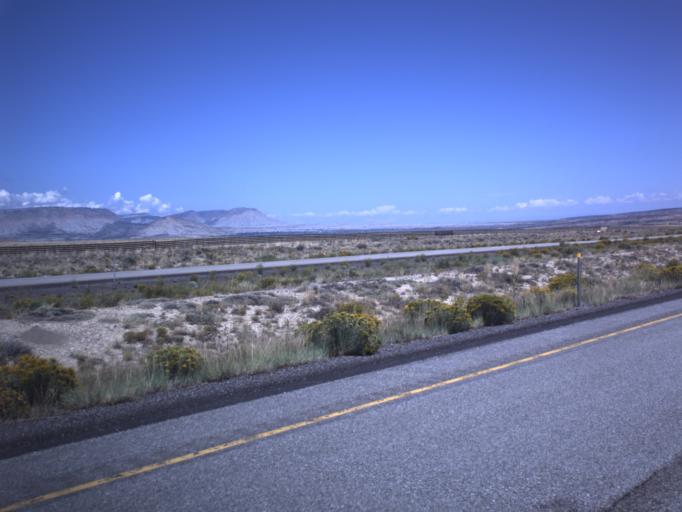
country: US
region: Utah
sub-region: Emery County
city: Ferron
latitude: 38.7733
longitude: -111.3283
